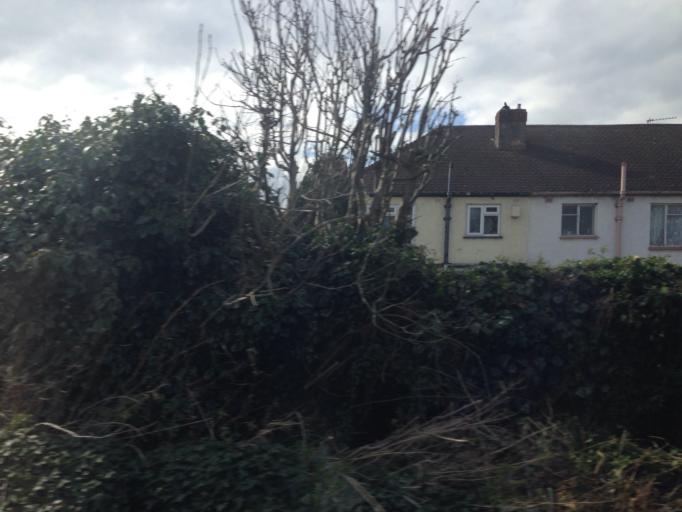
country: GB
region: England
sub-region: Greater London
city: Mitcham
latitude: 51.4034
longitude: -0.1574
